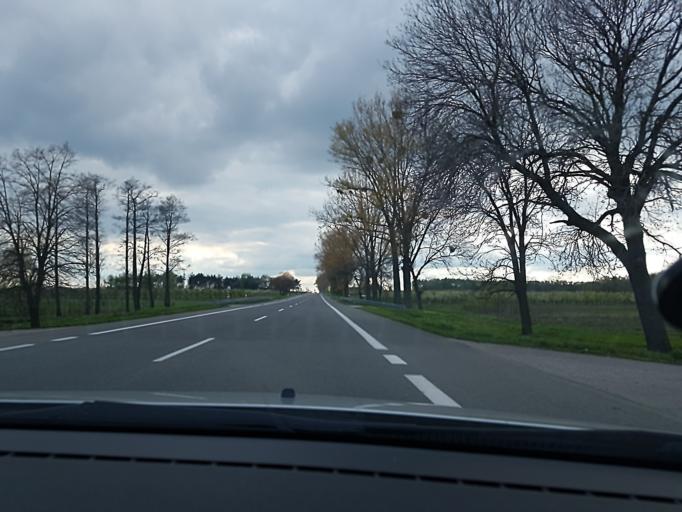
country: PL
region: Lodz Voivodeship
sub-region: powiat Lowicki
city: Nieborow
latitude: 52.1325
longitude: 20.0389
